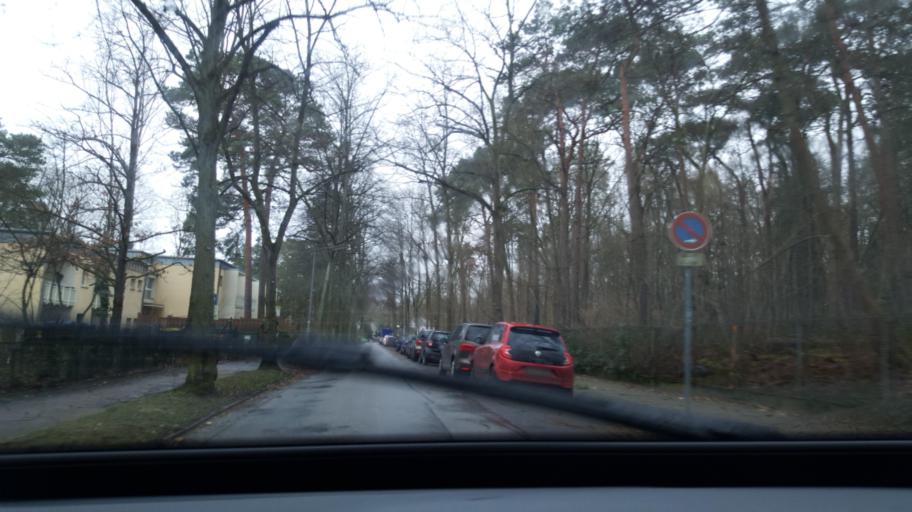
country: DE
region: Berlin
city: Wannsee
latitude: 52.4290
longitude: 13.1603
